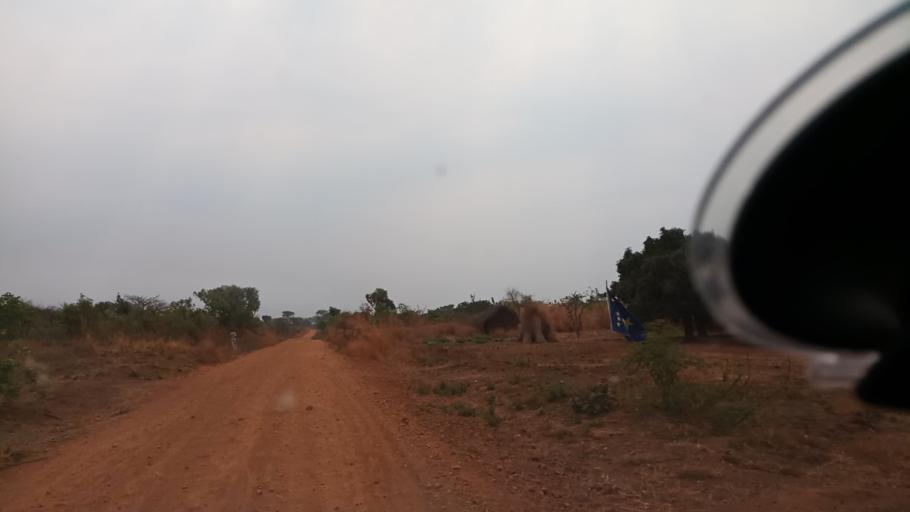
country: ZM
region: Luapula
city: Nchelenge
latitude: -9.0970
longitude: 28.3210
